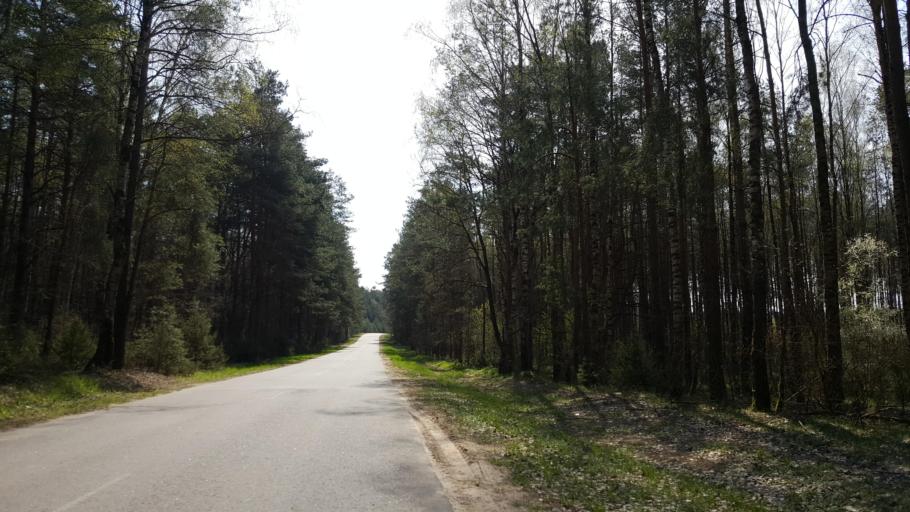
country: BY
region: Brest
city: Kamyanyets
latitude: 52.3602
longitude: 23.8173
